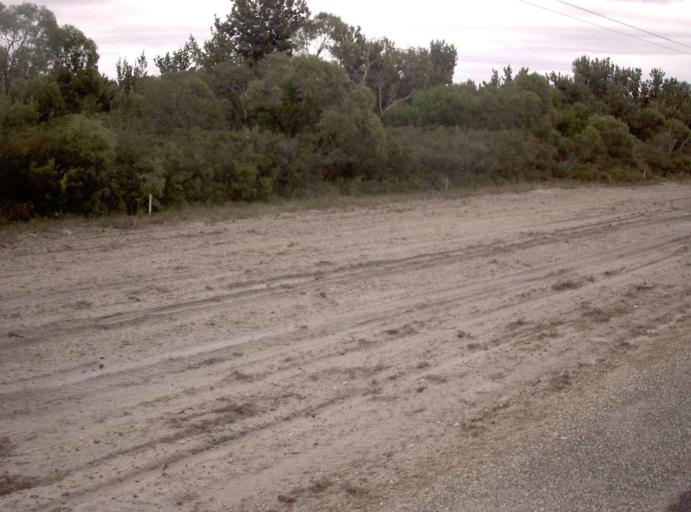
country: AU
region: Victoria
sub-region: East Gippsland
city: Bairnsdale
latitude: -38.0924
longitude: 147.5172
